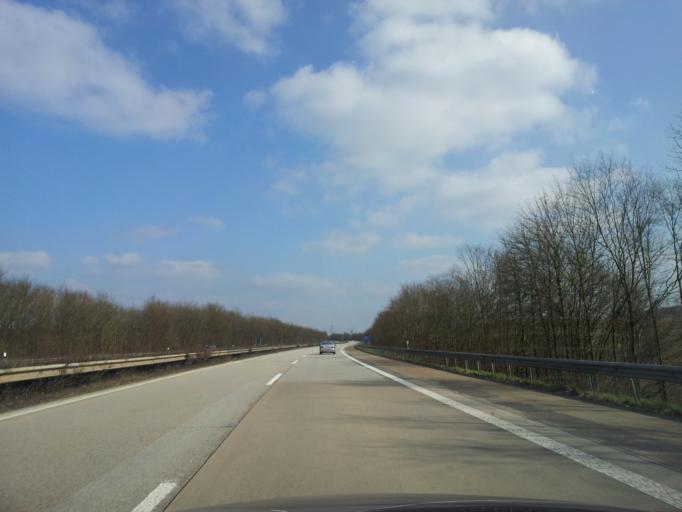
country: DE
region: Rheinland-Pfalz
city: Salmtal
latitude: 49.9250
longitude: 6.8620
